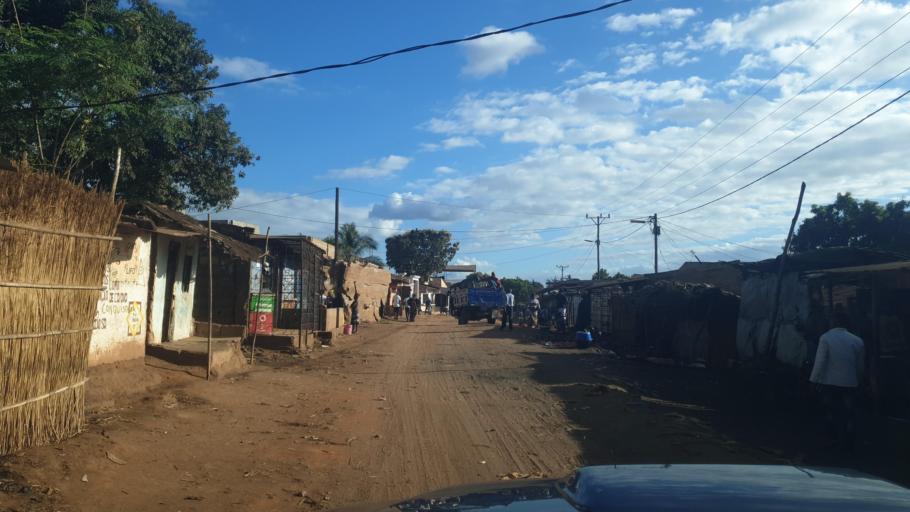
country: MZ
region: Nampula
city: Nampula
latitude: -15.1368
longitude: 39.2686
